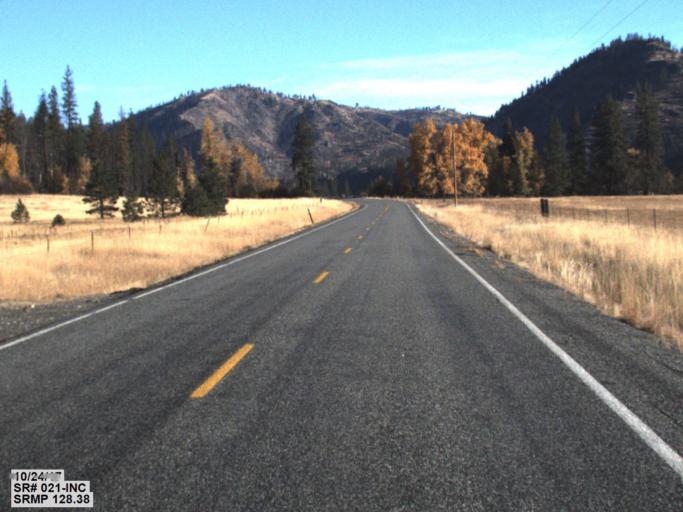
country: US
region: Washington
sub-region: Okanogan County
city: Coulee Dam
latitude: 48.2378
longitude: -118.6962
